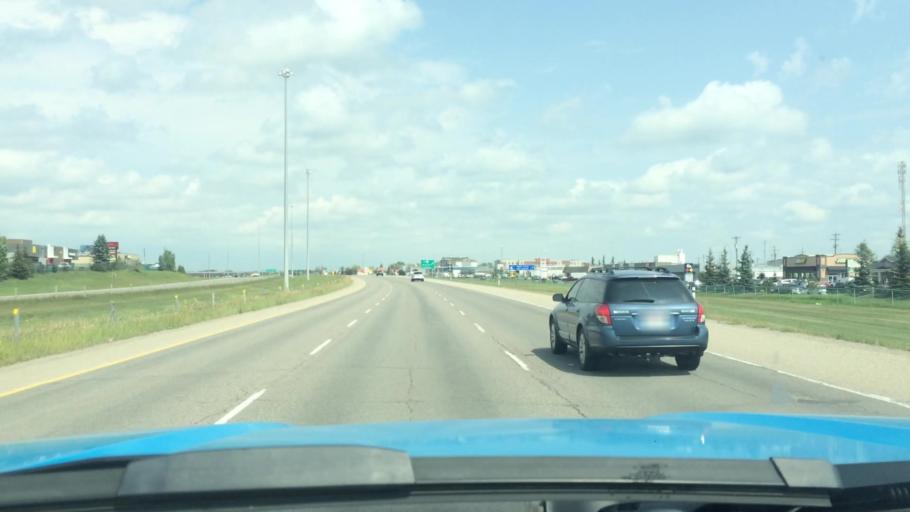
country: CA
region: Alberta
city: Airdrie
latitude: 51.2891
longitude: -113.9999
